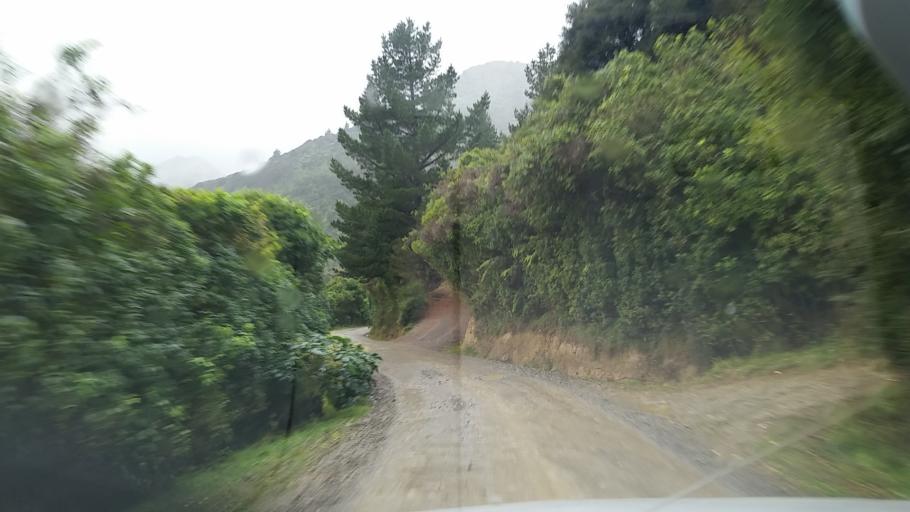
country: NZ
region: Marlborough
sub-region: Marlborough District
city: Picton
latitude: -41.1701
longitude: 174.0457
